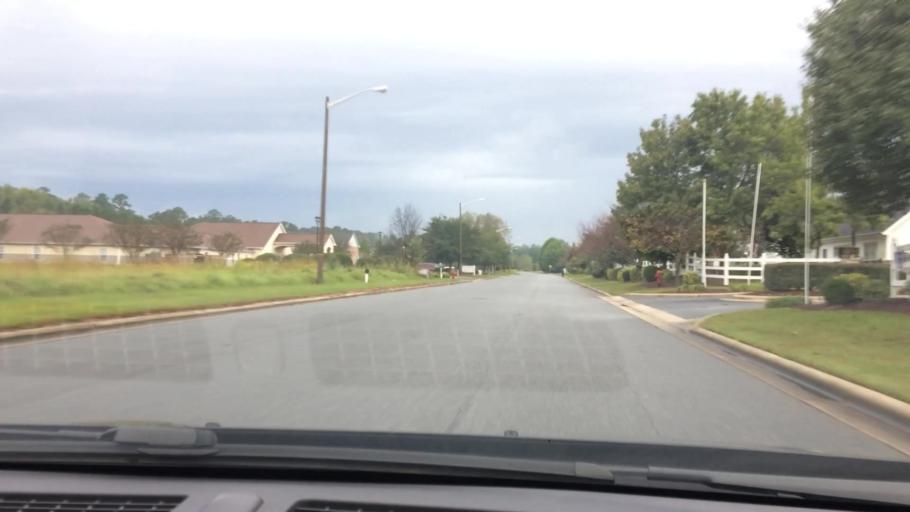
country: US
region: North Carolina
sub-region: Pitt County
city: Windsor
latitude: 35.5653
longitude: -77.3633
